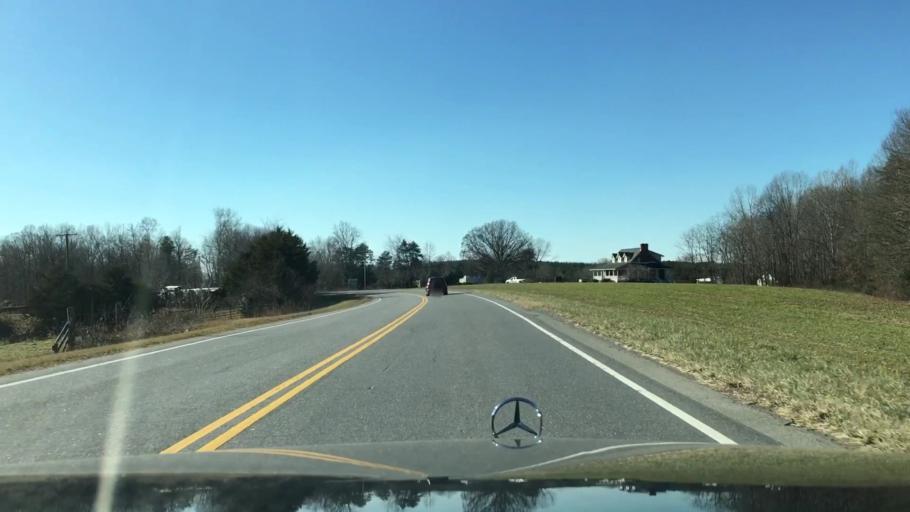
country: US
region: Virginia
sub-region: City of Bedford
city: Bedford
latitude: 37.2125
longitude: -79.4384
